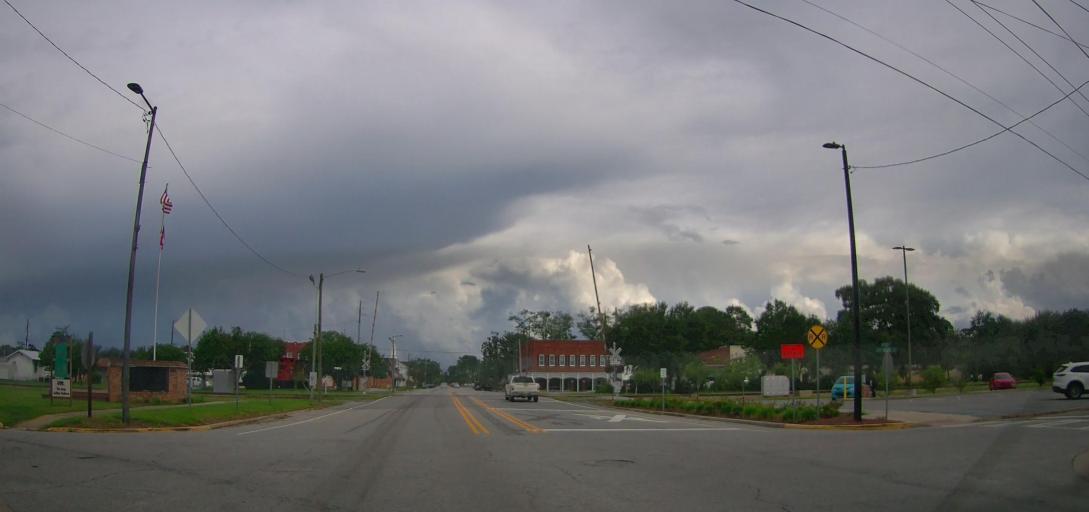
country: US
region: Georgia
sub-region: Wayne County
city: Jesup
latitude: 31.6054
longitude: -81.8831
